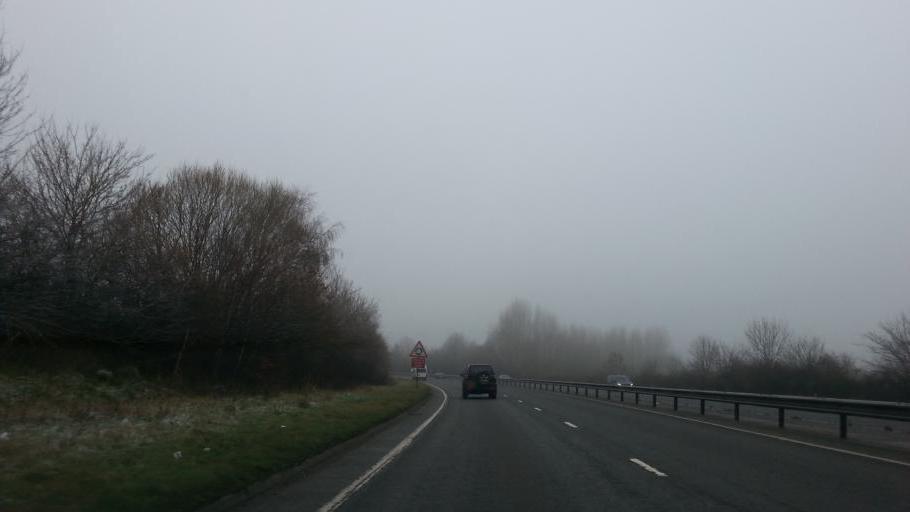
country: GB
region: England
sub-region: Cheshire East
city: Wilmslow
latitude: 53.3162
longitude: -2.2271
